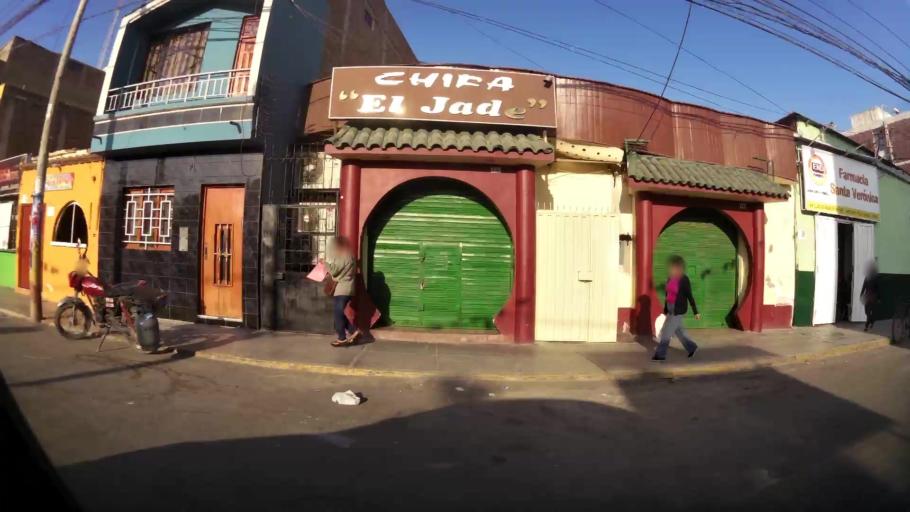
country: PE
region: Lambayeque
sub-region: Provincia de Chiclayo
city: Chiclayo
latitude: -6.7747
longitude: -79.8425
